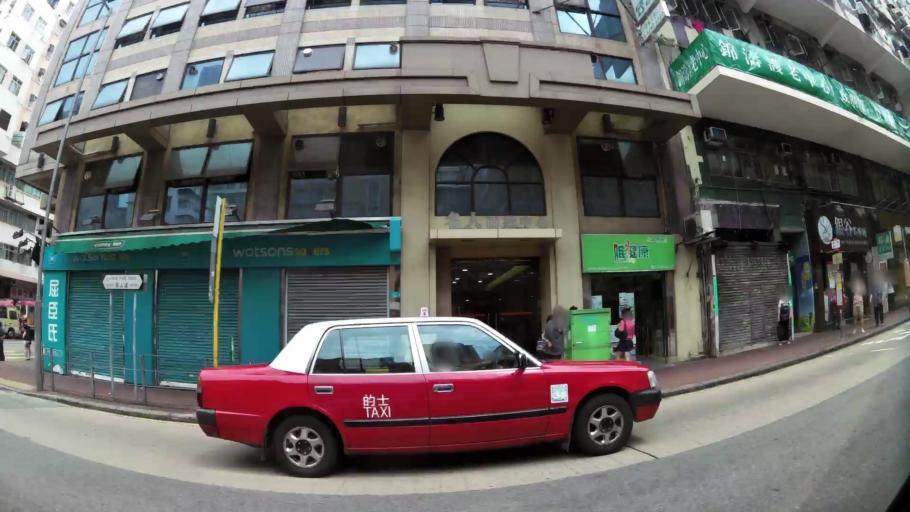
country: HK
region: Sham Shui Po
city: Sham Shui Po
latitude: 22.3342
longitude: 114.1618
